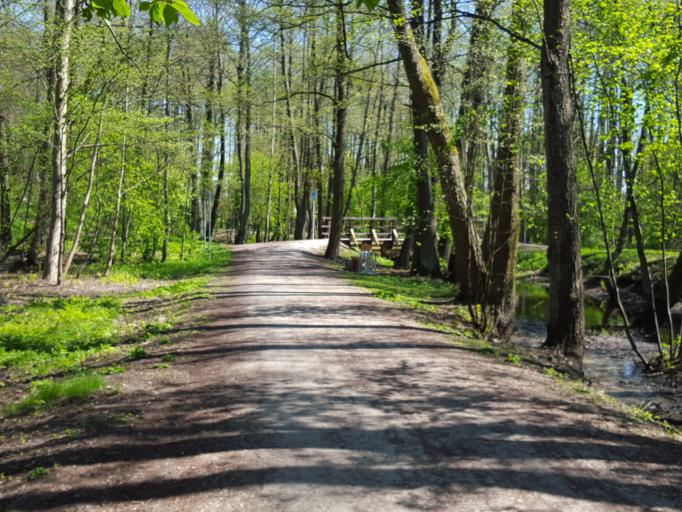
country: LV
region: Marupe
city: Marupe
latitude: 56.9178
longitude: 24.0612
